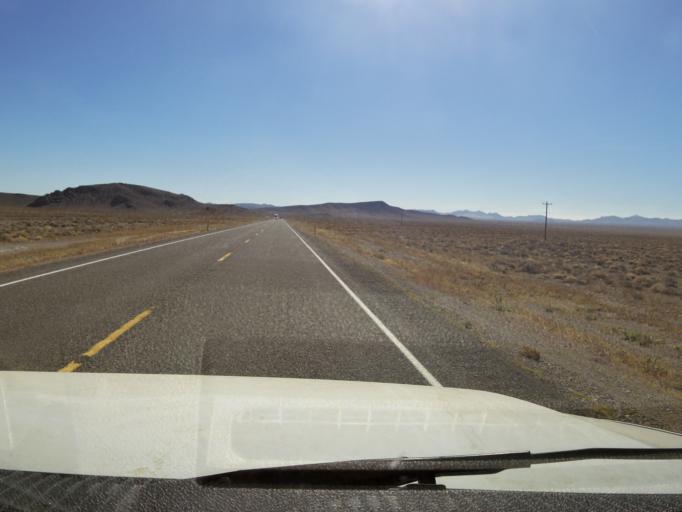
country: US
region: Nevada
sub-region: Nye County
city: Beatty
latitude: 37.1972
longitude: -116.9504
